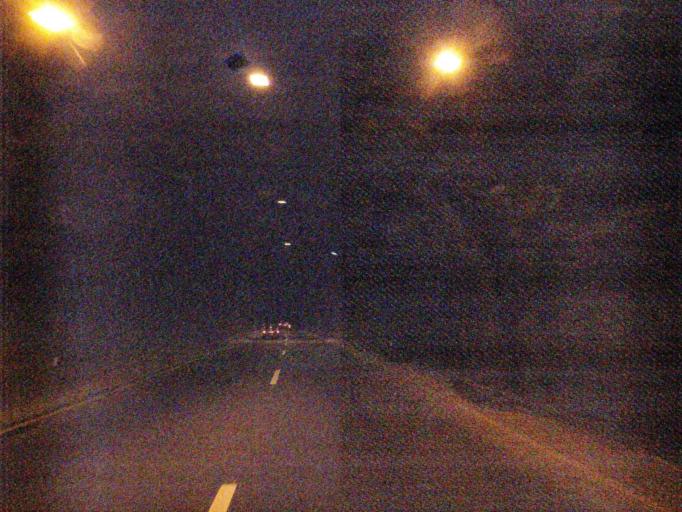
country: BR
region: Rio de Janeiro
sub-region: Rio De Janeiro
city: Rio de Janeiro
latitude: -22.9840
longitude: -43.2386
